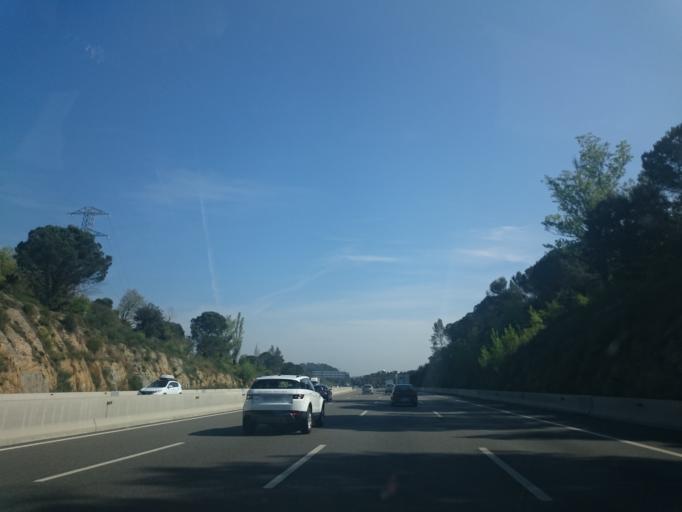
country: ES
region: Catalonia
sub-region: Provincia de Girona
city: Girona
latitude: 42.0034
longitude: 2.8060
